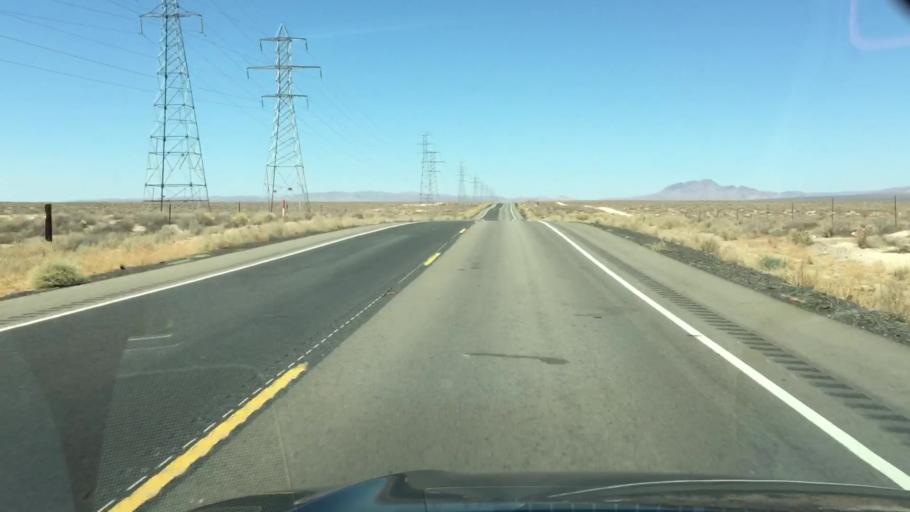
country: US
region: California
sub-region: Kern County
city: Boron
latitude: 35.1226
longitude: -117.5779
